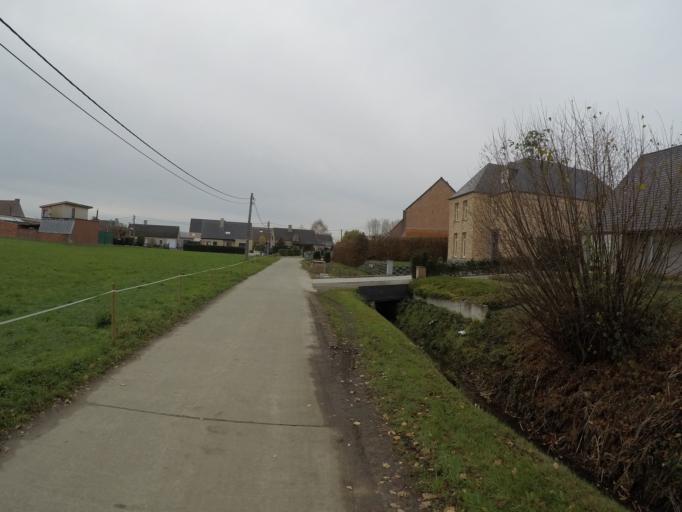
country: BE
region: Flanders
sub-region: Provincie Antwerpen
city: Berlaar
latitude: 51.1121
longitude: 4.6716
